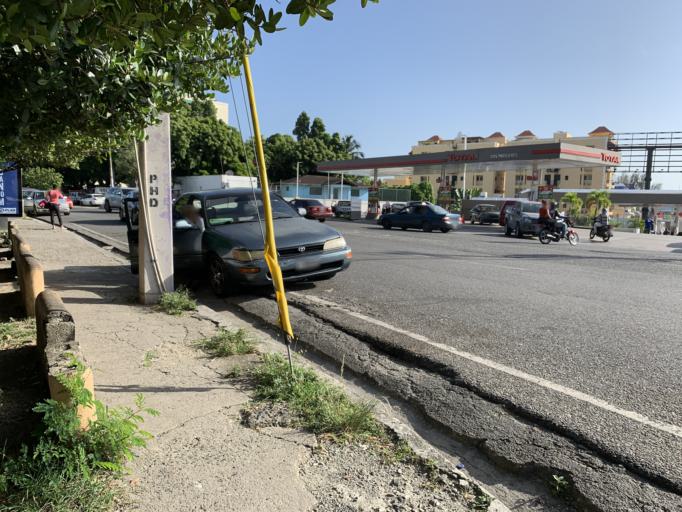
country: DO
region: Nacional
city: Santo Domingo
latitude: 18.4841
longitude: -69.9677
